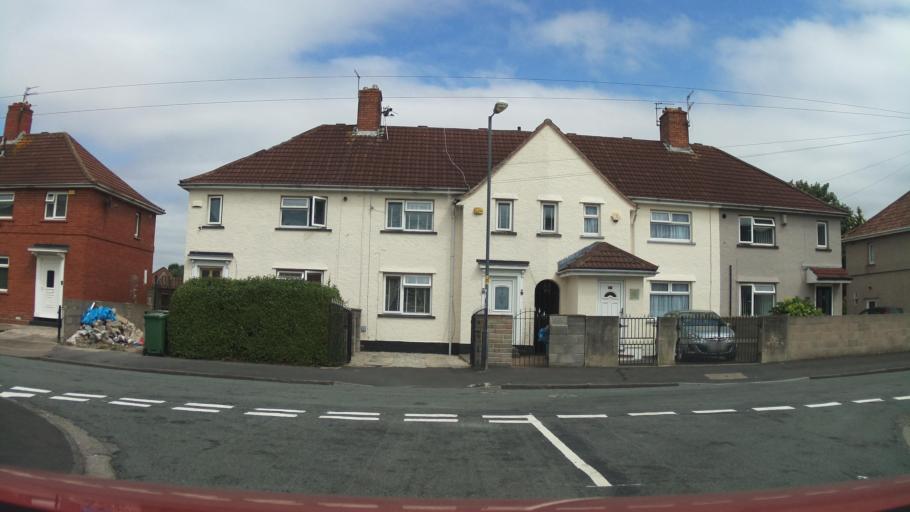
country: GB
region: England
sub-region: Bristol
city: Bristol
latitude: 51.4296
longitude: -2.5858
